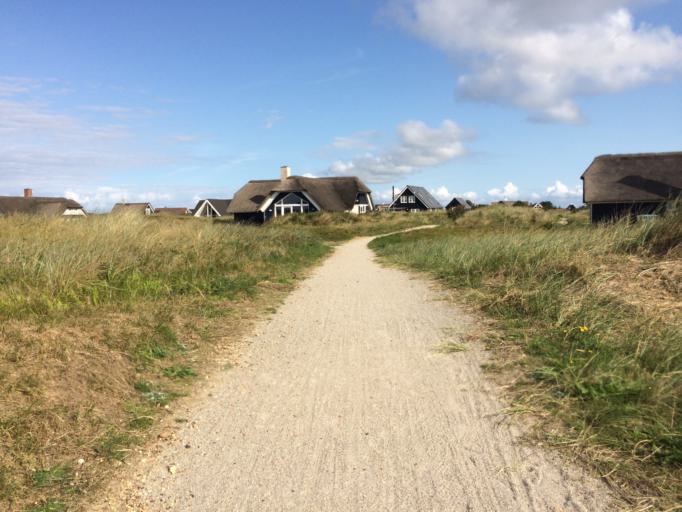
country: DK
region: Central Jutland
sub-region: Ringkobing-Skjern Kommune
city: Hvide Sande
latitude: 55.8854
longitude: 8.1684
